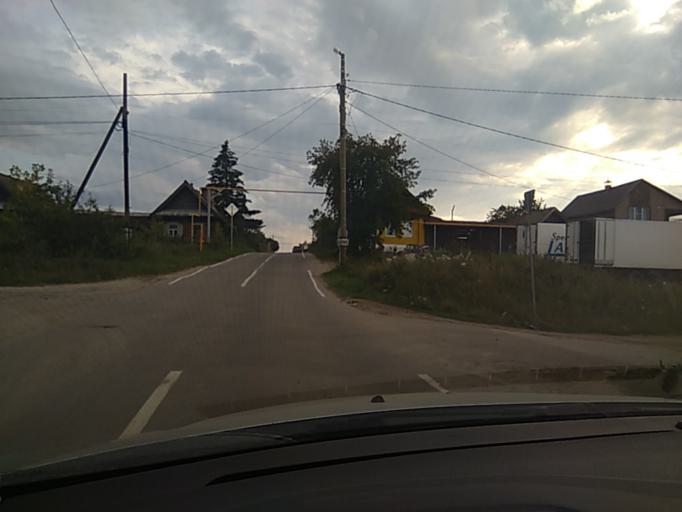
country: RU
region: Chelyabinsk
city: Kyshtym
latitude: 55.6992
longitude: 60.5309
